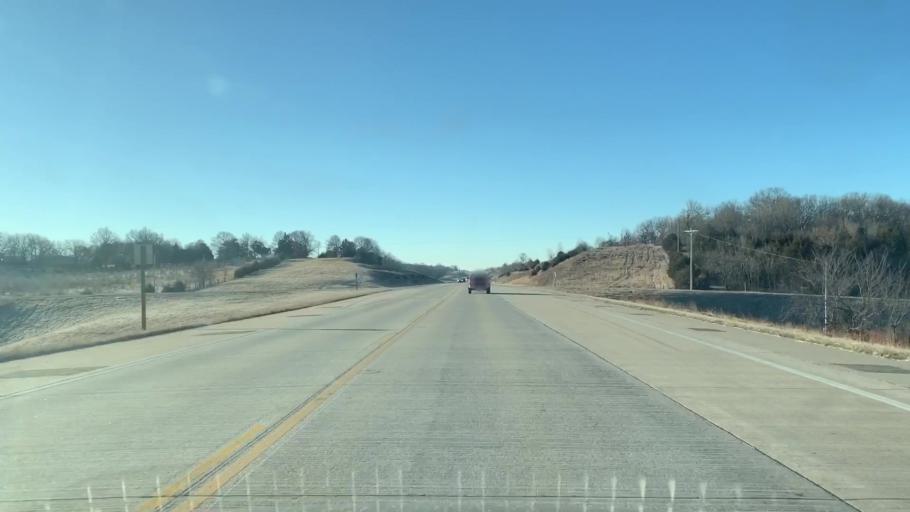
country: US
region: Kansas
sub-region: Crawford County
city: Arma
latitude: 37.6307
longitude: -94.7040
